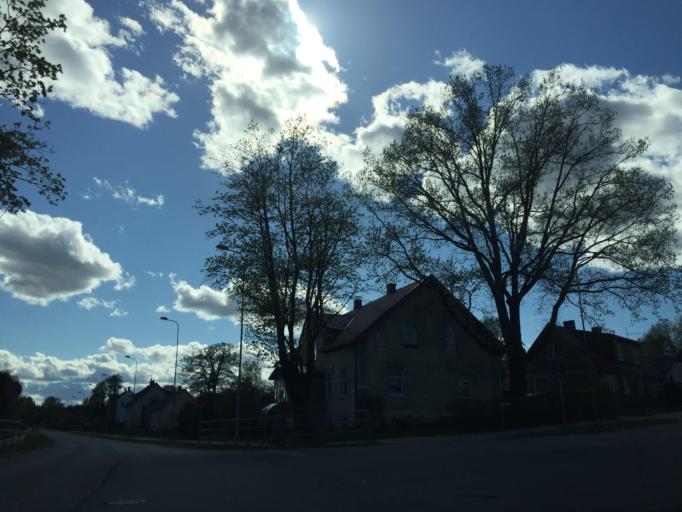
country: LV
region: Madonas Rajons
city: Madona
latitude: 56.8487
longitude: 26.2136
